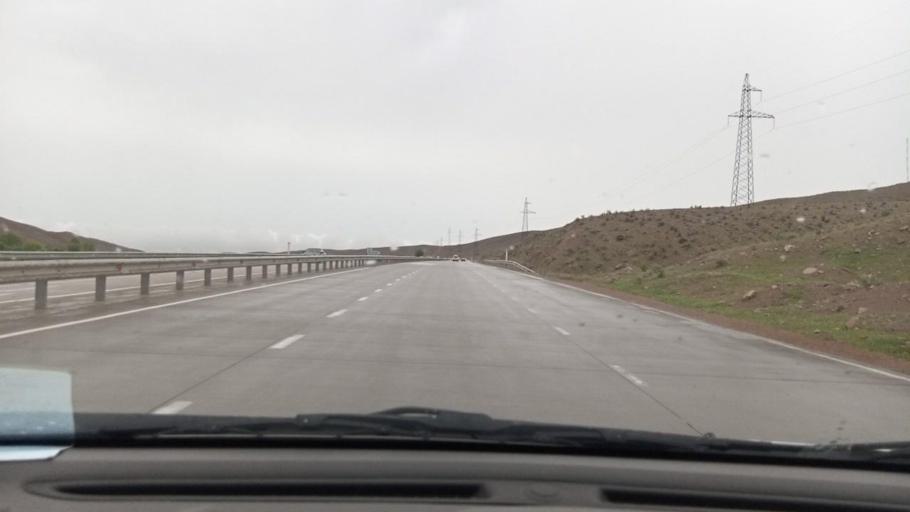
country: UZ
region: Namangan
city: Pop Shahri
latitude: 40.9406
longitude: 70.6904
